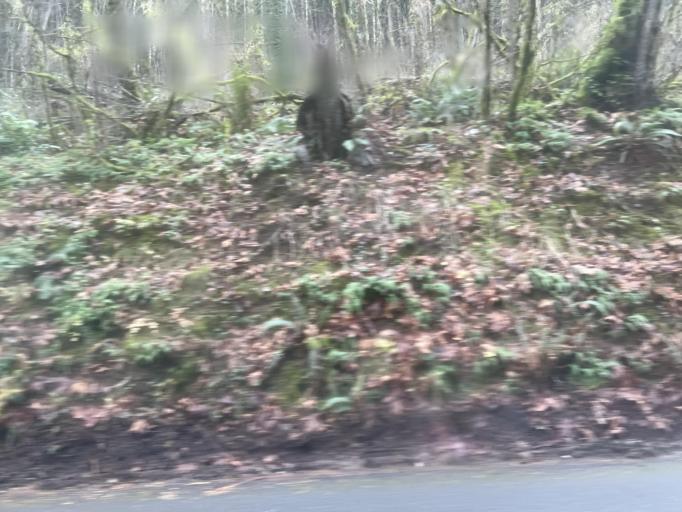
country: US
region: Washington
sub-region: Clark County
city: Washougal
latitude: 45.5518
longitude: -122.1869
